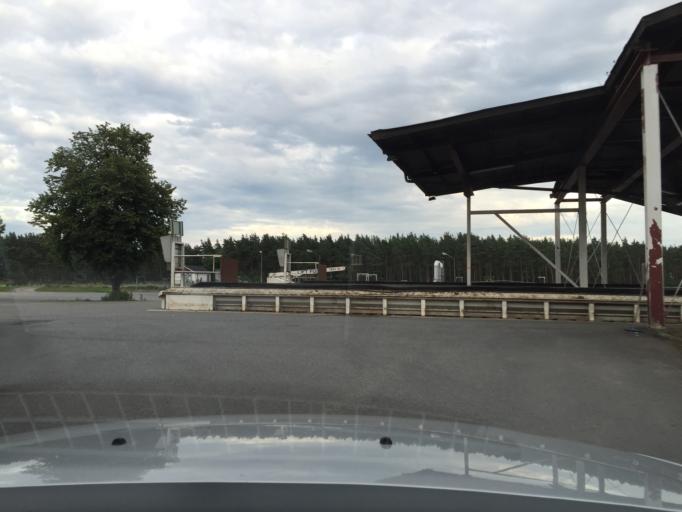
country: SE
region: Skane
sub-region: Kristianstads Kommun
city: Norra Asum
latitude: 55.9464
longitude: 14.0652
